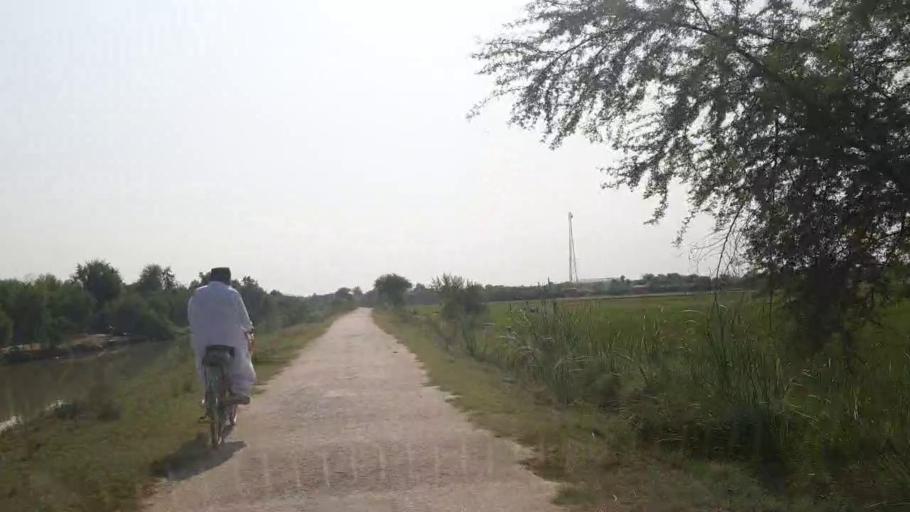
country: PK
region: Sindh
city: Badin
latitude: 24.6422
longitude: 68.8484
